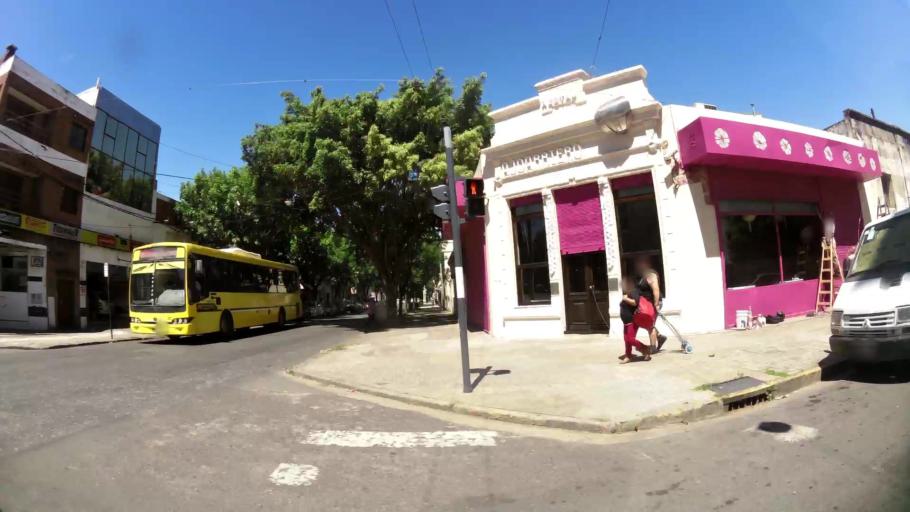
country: AR
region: Santa Fe
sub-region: Departamento de Rosario
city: Rosario
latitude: -32.9362
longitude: -60.6613
